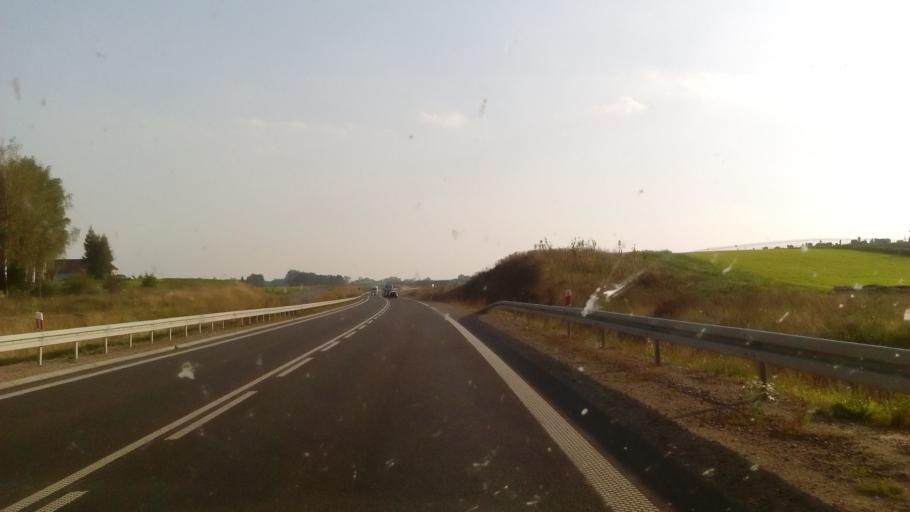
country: PL
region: Podlasie
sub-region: Powiat grajewski
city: Rajgrod
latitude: 53.7740
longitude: 22.8346
